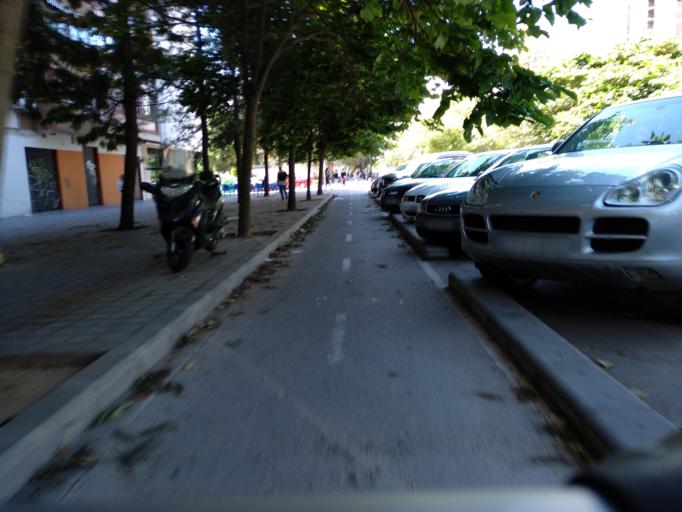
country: ES
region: Valencia
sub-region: Provincia de Valencia
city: Alboraya
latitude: 39.4782
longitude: -0.3543
